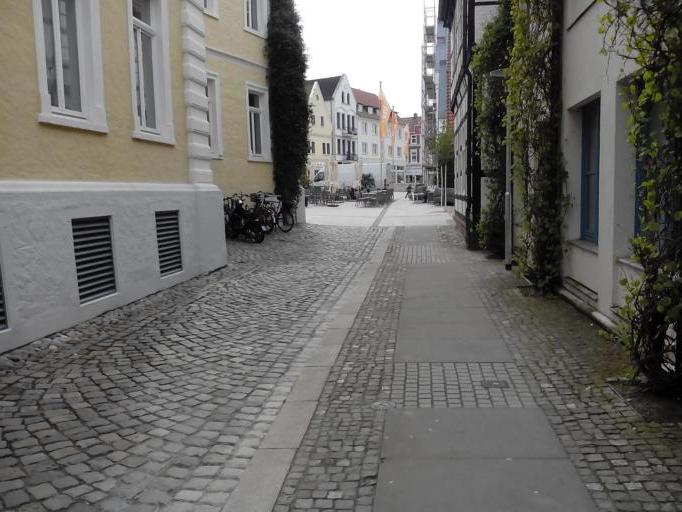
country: DE
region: Lower Saxony
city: Verden
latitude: 52.9223
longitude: 9.2279
